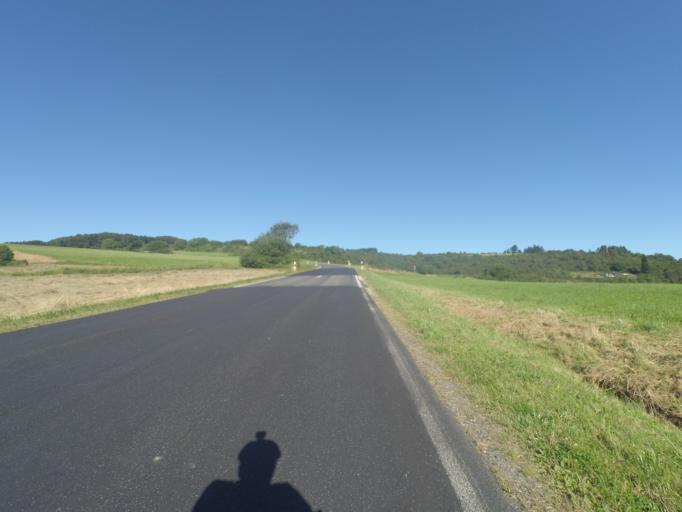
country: DE
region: Rheinland-Pfalz
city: Oberstadtfeld
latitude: 50.2010
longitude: 6.7852
